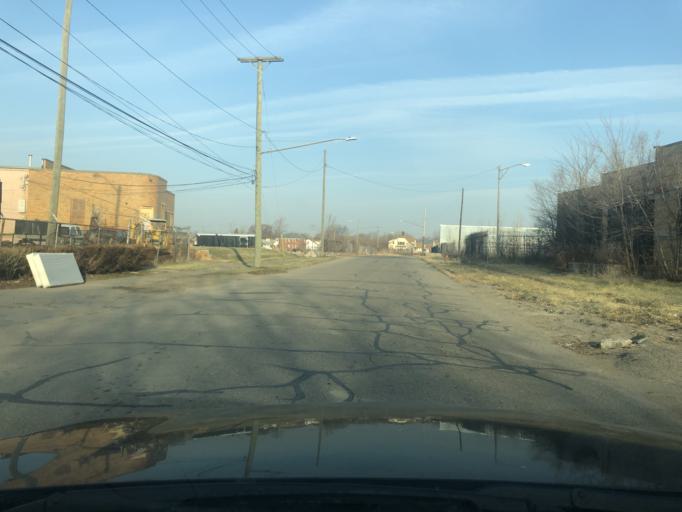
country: US
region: Michigan
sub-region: Wayne County
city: Highland Park
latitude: 42.3969
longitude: -83.1317
